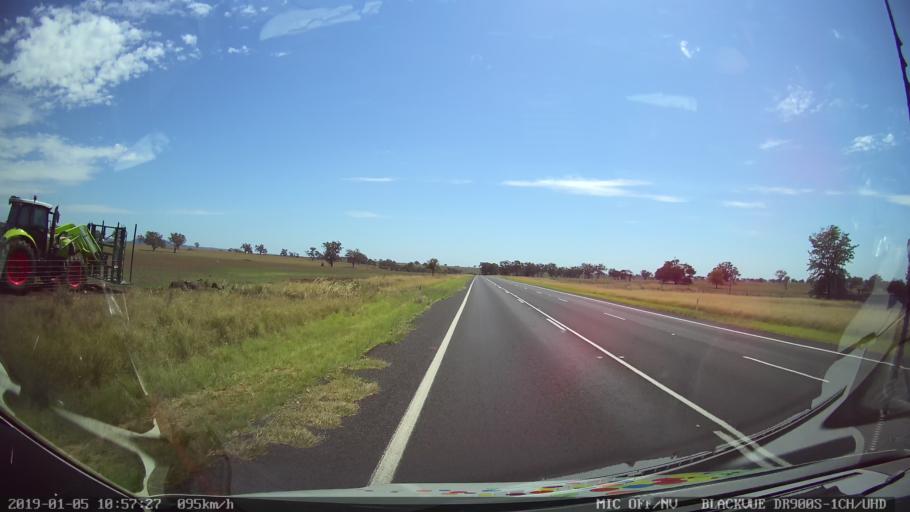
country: AU
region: New South Wales
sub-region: Warrumbungle Shire
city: Coonabarabran
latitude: -31.4312
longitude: 149.1698
